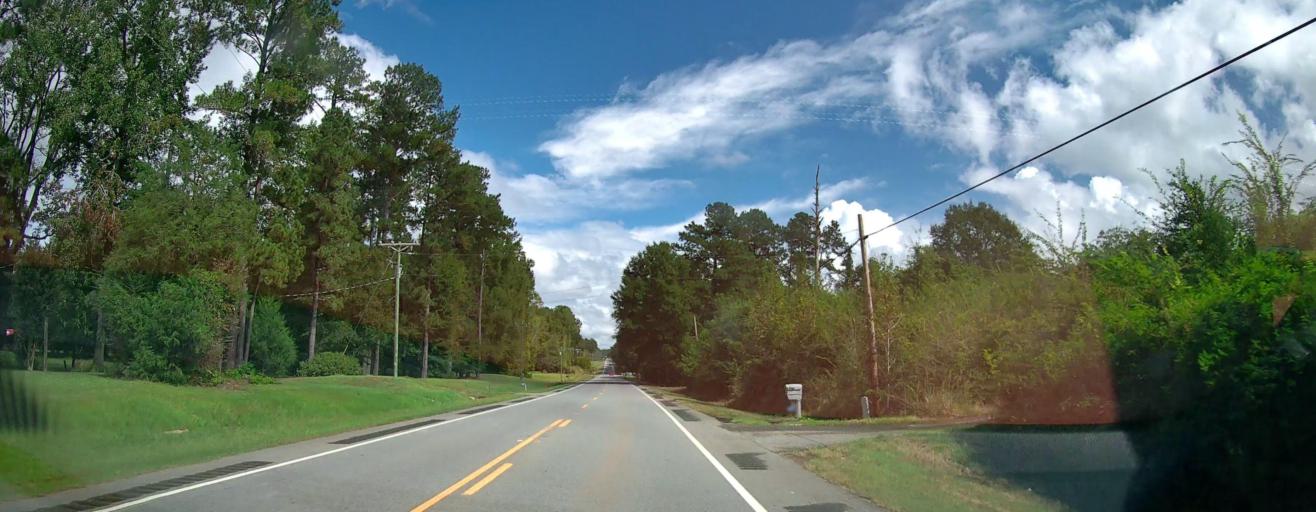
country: US
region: Georgia
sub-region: Baldwin County
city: Milledgeville
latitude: 33.0320
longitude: -83.3174
